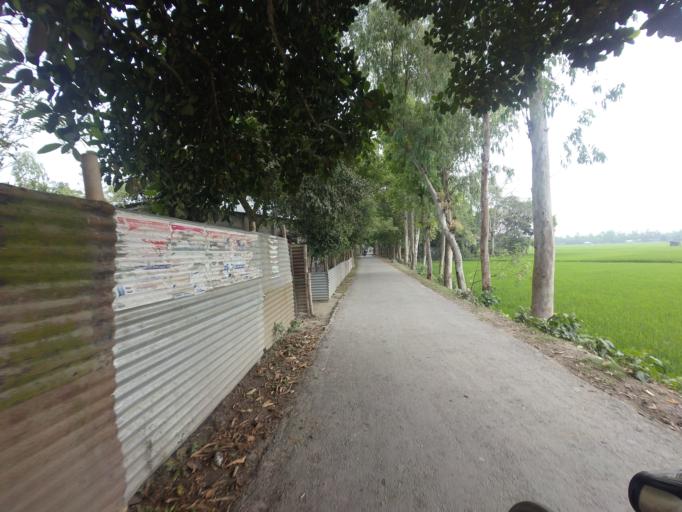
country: BD
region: Rajshahi
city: Sirajganj
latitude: 24.3245
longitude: 89.6755
